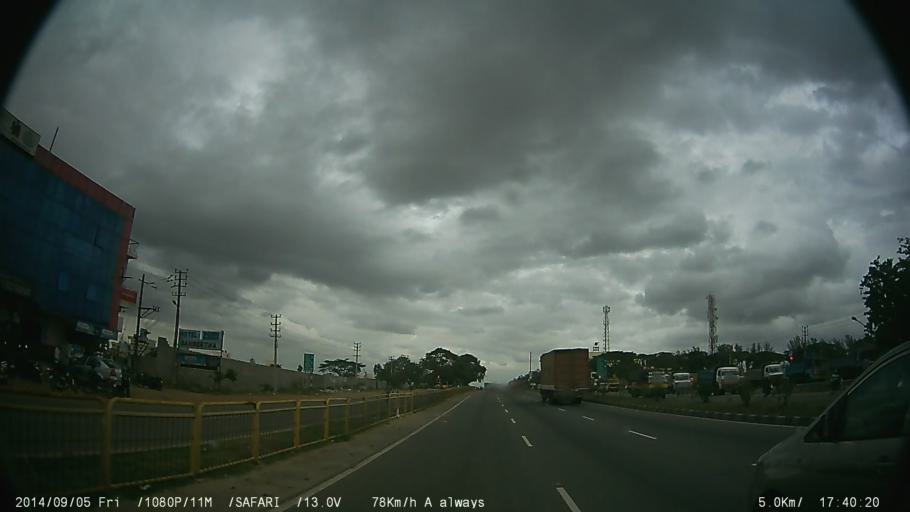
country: IN
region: Karnataka
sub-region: Bangalore Urban
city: Anekal
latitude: 12.7873
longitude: 77.7402
